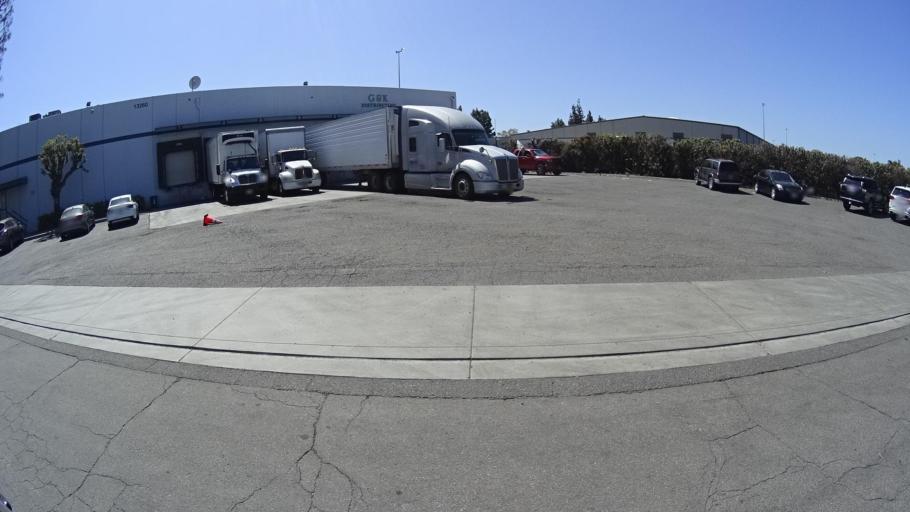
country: US
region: California
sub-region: Los Angeles County
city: West Puente Valley
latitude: 34.0624
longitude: -117.9855
